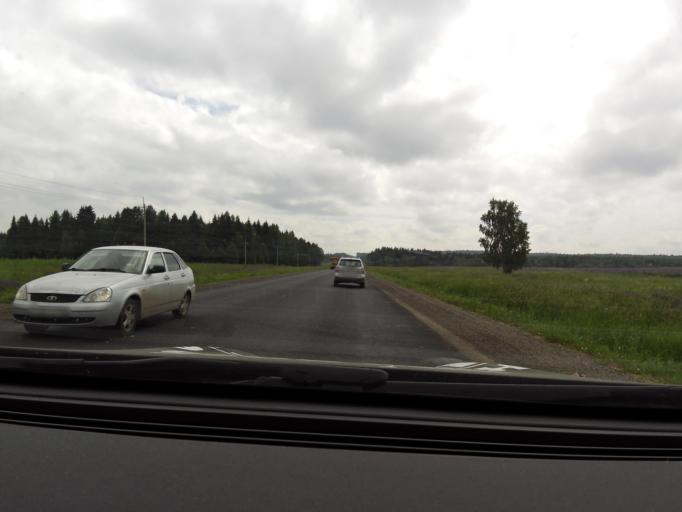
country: RU
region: Perm
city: Bershet'
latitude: 57.7740
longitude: 56.3500
